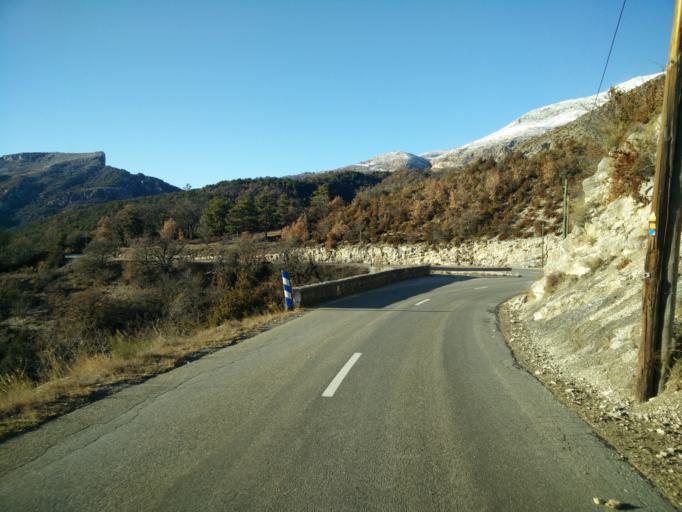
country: FR
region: Provence-Alpes-Cote d'Azur
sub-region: Departement des Alpes-de-Haute-Provence
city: Castellane
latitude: 43.7944
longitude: 6.3893
